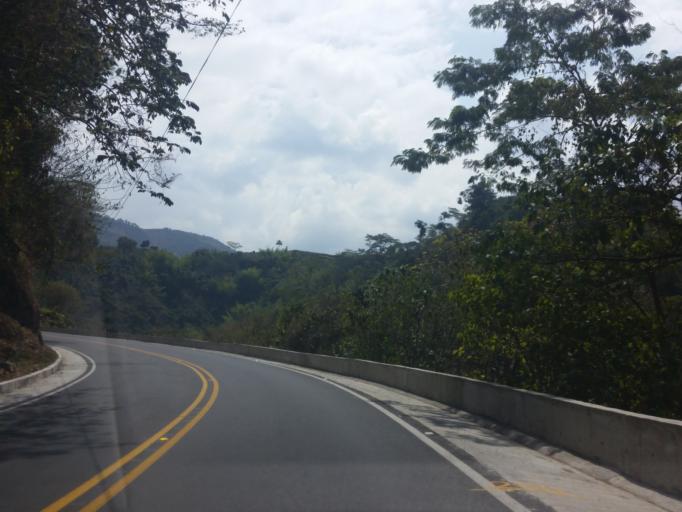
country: CO
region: Caldas
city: Chinchina
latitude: 4.9852
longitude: -75.5887
